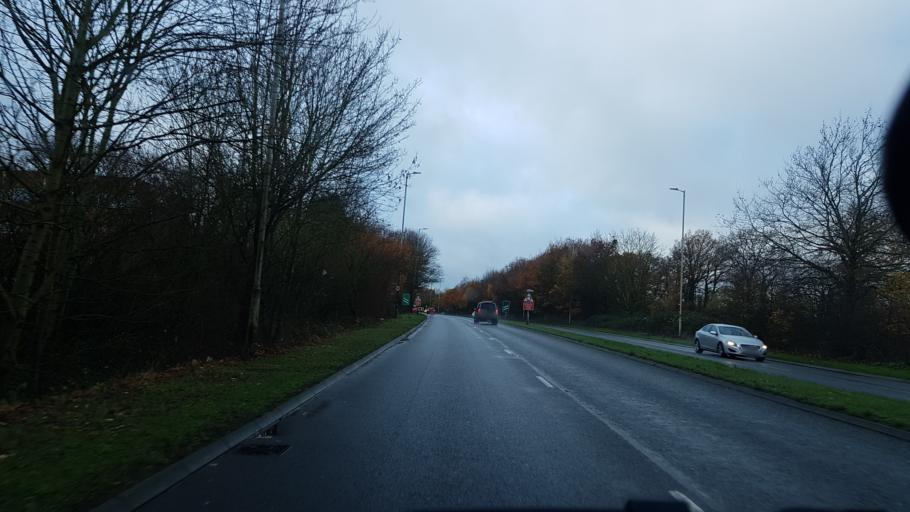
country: GB
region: England
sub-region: Bracknell Forest
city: Bracknell
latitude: 51.4136
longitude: -0.7701
